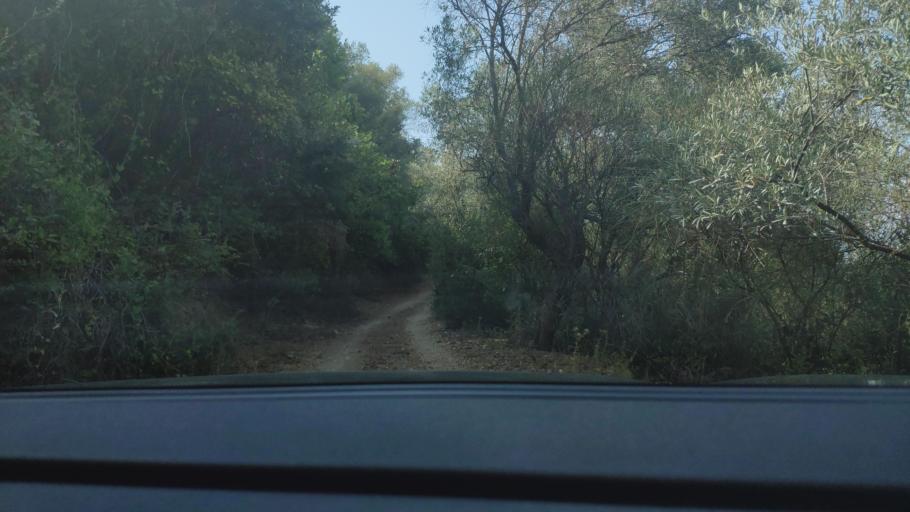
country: GR
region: West Greece
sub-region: Nomos Aitolias kai Akarnanias
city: Fitiai
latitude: 38.7330
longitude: 21.1828
